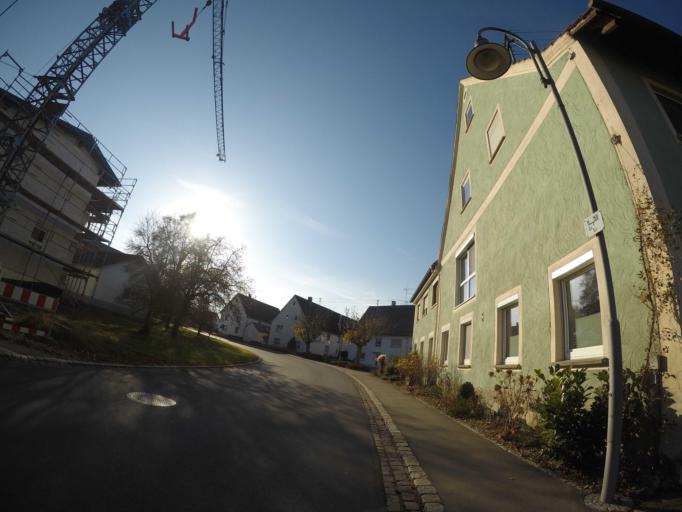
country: DE
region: Baden-Wuerttemberg
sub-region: Tuebingen Region
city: Emerkingen
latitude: 48.1932
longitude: 9.6641
